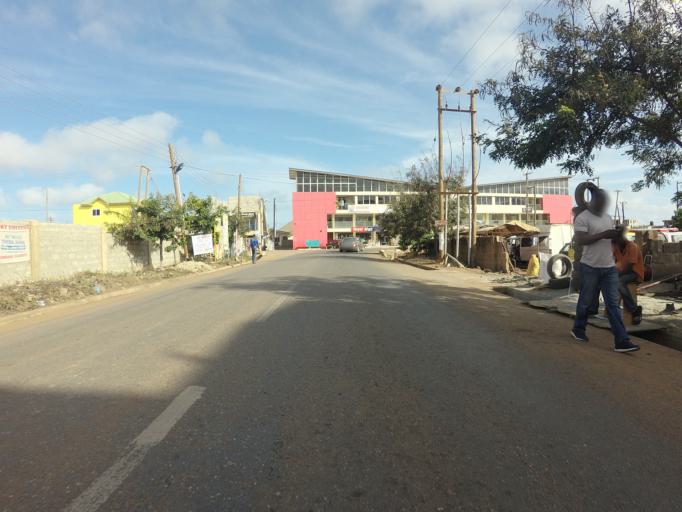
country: GH
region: Greater Accra
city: Teshi Old Town
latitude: 5.5761
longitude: -0.1386
